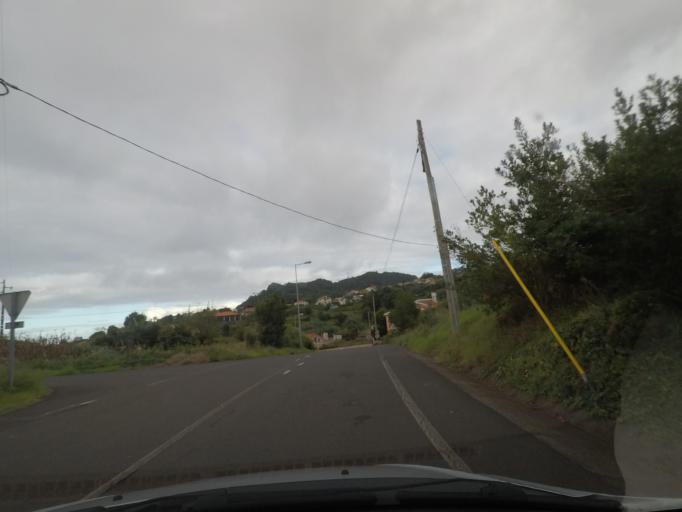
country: PT
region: Madeira
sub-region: Santana
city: Santana
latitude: 32.8115
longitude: -16.8834
